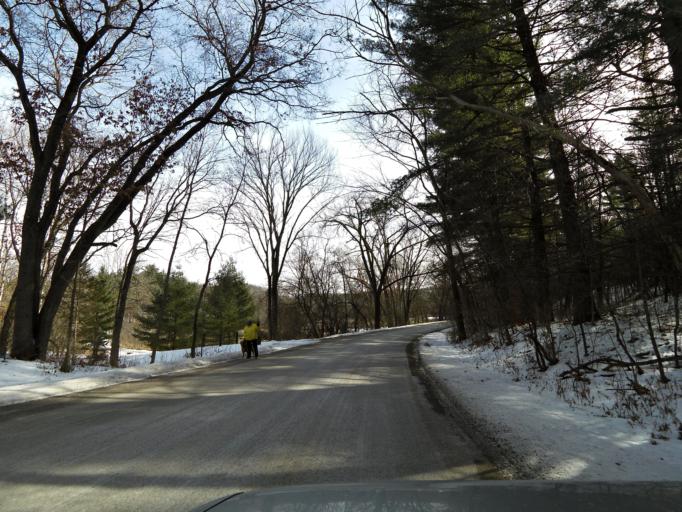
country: US
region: Minnesota
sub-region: Washington County
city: Afton
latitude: 44.9409
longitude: -92.8309
